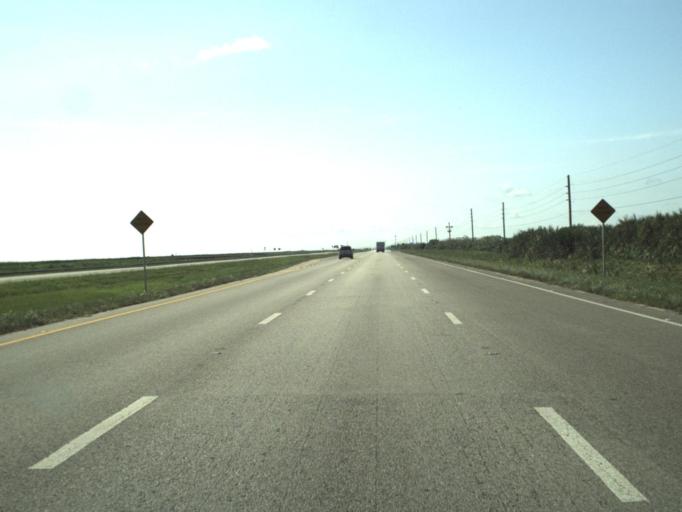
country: US
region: Florida
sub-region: Palm Beach County
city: Belle Glade Camp
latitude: 26.4306
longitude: -80.6121
